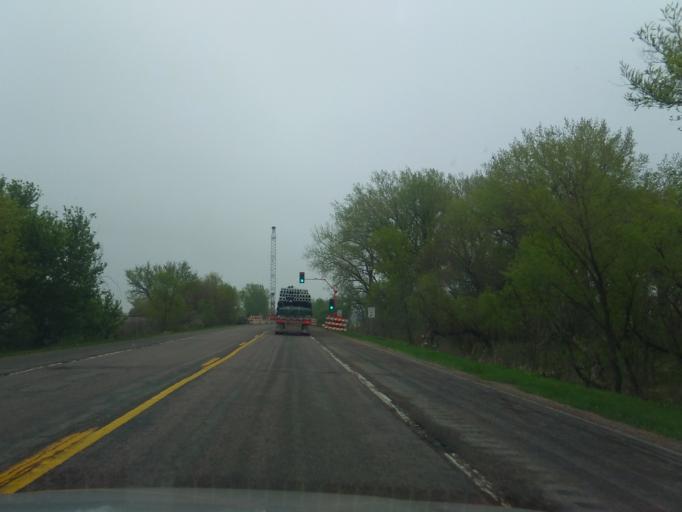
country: US
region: Nebraska
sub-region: Burt County
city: Oakland
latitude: 41.8075
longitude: -96.4780
